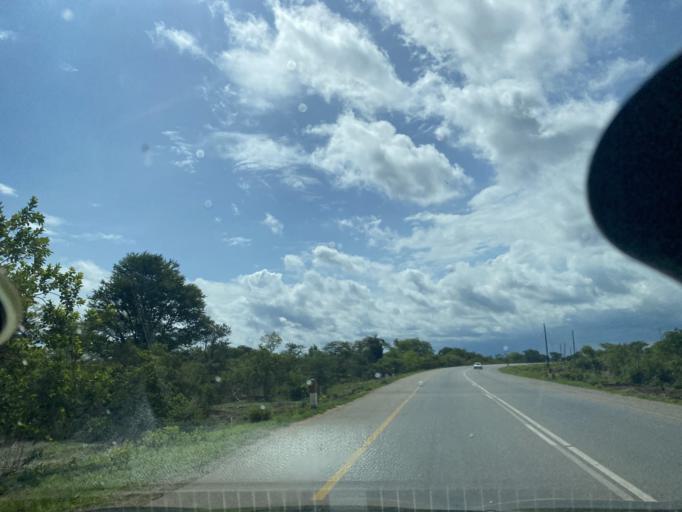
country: ZM
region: Lusaka
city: Kafue
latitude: -15.8579
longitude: 28.2617
